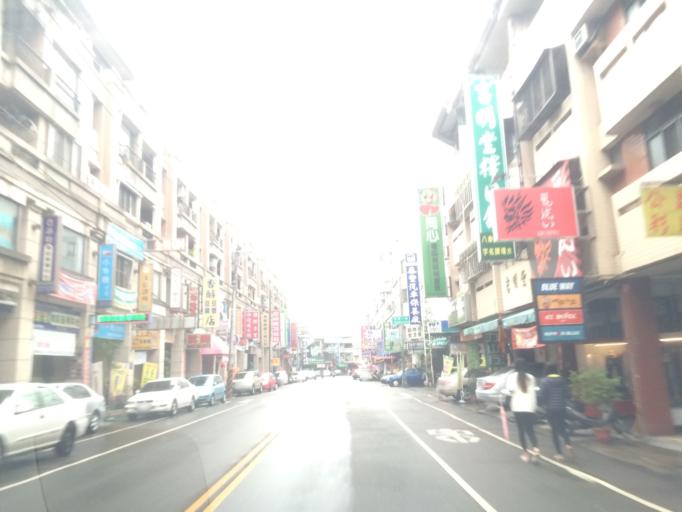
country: TW
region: Taiwan
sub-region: Taichung City
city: Taichung
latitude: 24.1802
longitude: 120.6899
